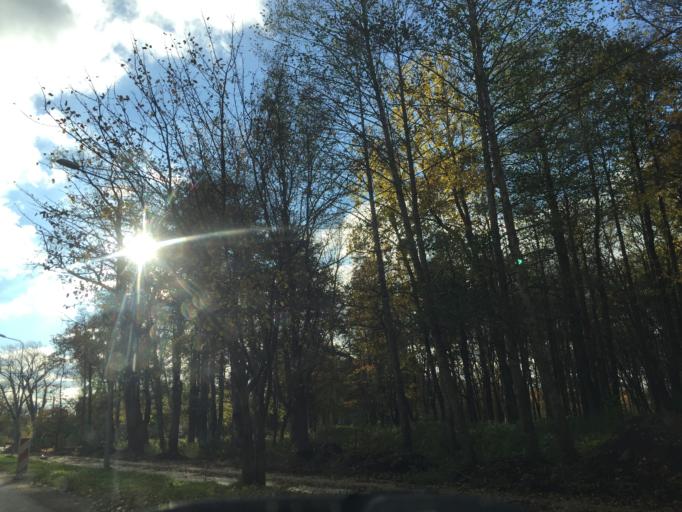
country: LV
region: Liepaja
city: Vec-Liepaja
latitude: 56.5425
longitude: 21.0789
